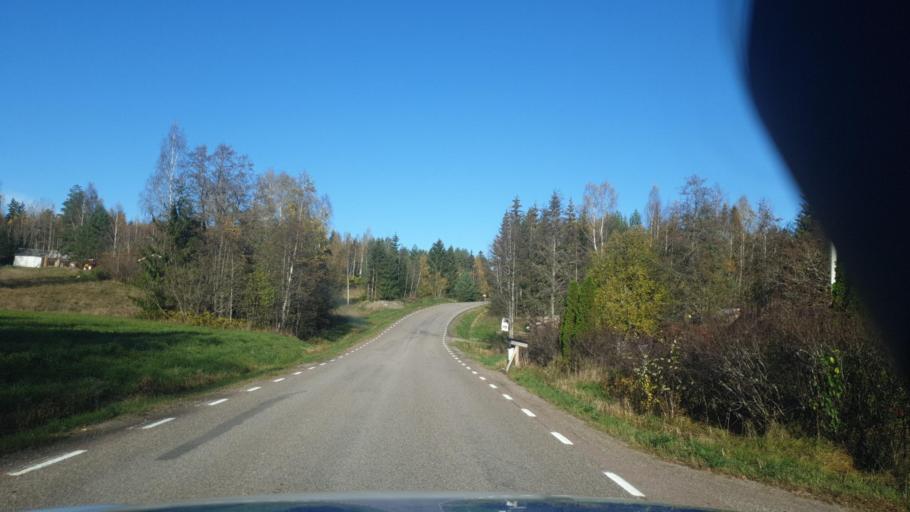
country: SE
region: Vaermland
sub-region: Arvika Kommun
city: Arvika
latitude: 59.6161
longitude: 12.7862
